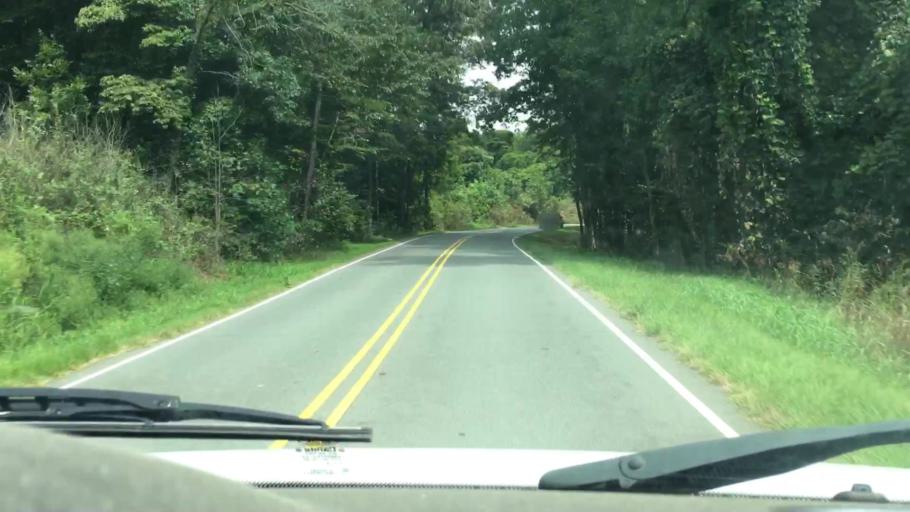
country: US
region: North Carolina
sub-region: Gaston County
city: Davidson
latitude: 35.5054
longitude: -80.8083
